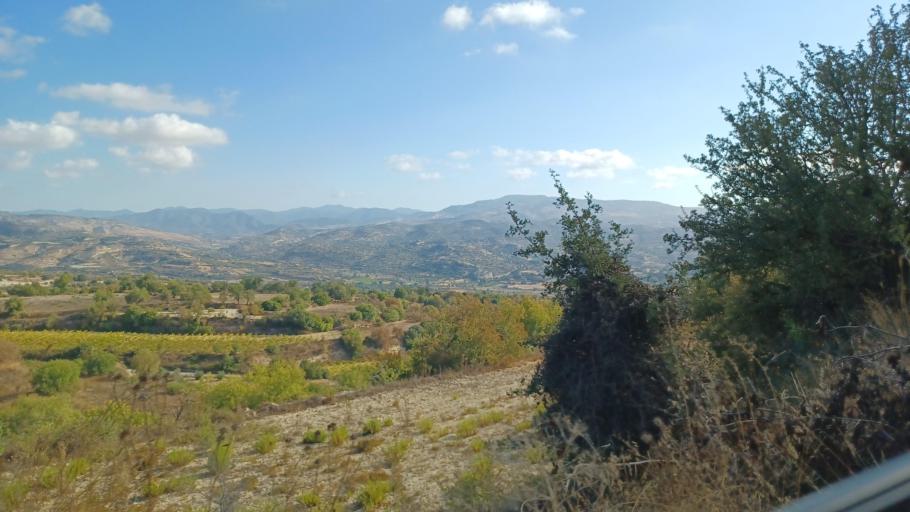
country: CY
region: Pafos
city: Mesogi
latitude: 34.8435
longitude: 32.5251
